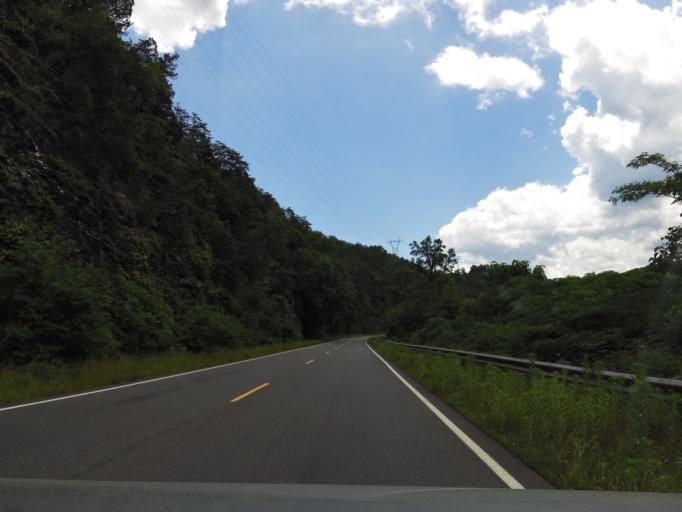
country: US
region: Tennessee
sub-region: Blount County
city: Maryville
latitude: 35.5507
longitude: -83.9926
